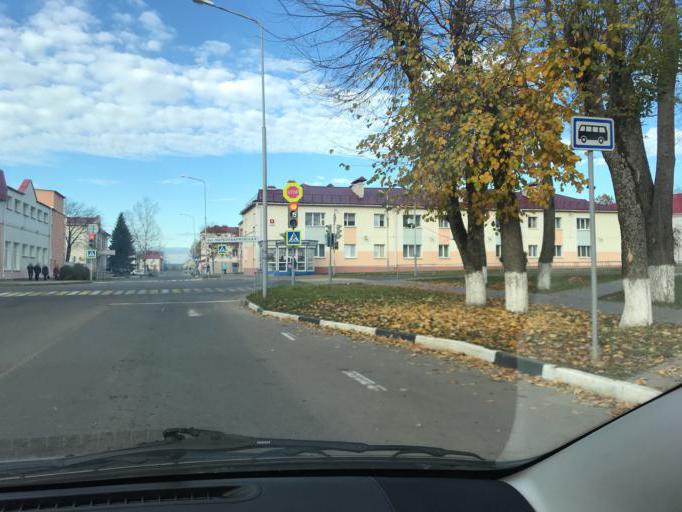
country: BY
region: Vitebsk
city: Haradok
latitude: 55.4602
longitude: 29.9875
